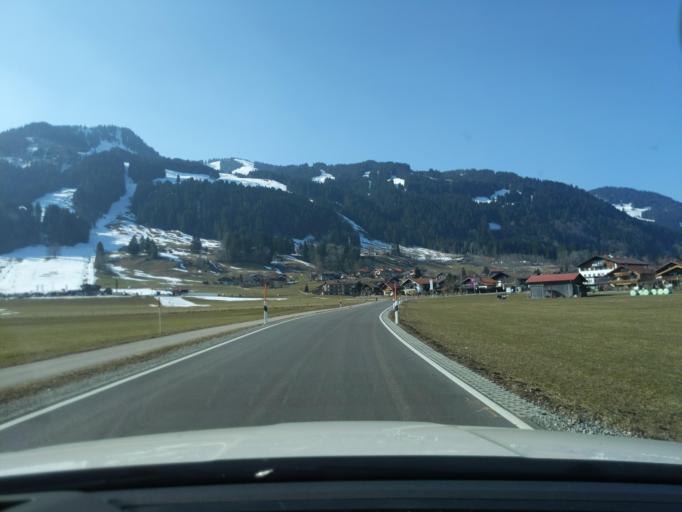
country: DE
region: Bavaria
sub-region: Swabia
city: Obermaiselstein
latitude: 47.4568
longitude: 10.2376
